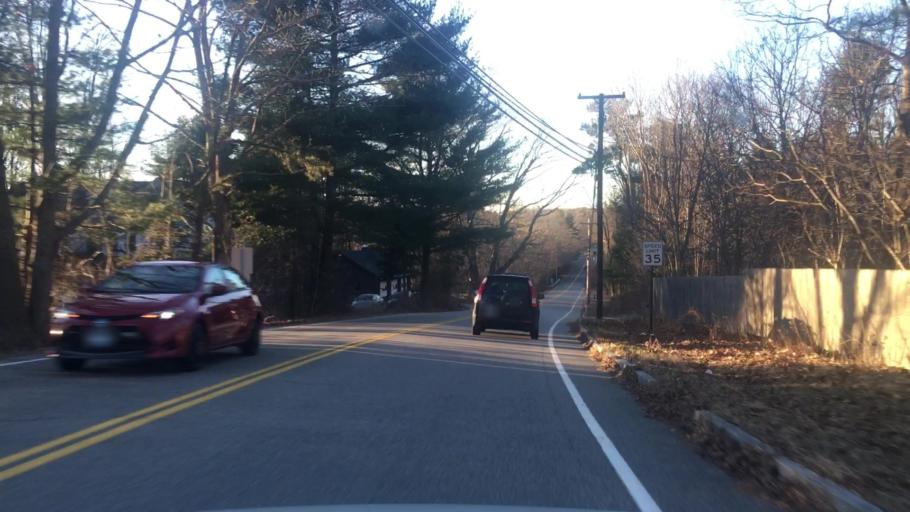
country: US
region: Maine
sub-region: York County
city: South Eliot
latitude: 43.1072
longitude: -70.7673
